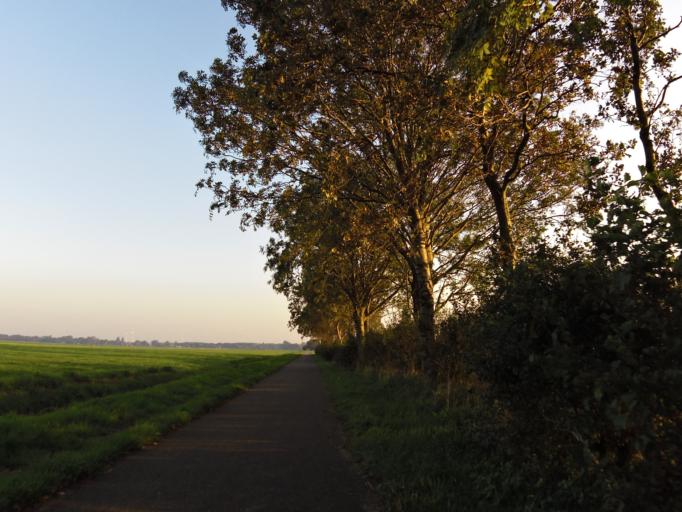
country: NL
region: South Holland
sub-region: Gemeente Leiderdorp
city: Leiderdorp
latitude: 52.1470
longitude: 4.5854
